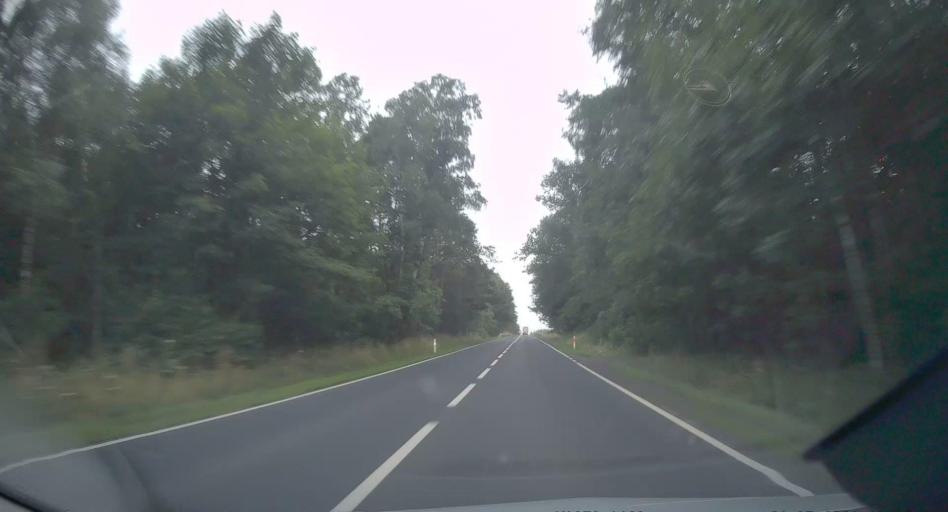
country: PL
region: Opole Voivodeship
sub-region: Powiat oleski
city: Dalachow
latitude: 51.1021
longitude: 18.6075
